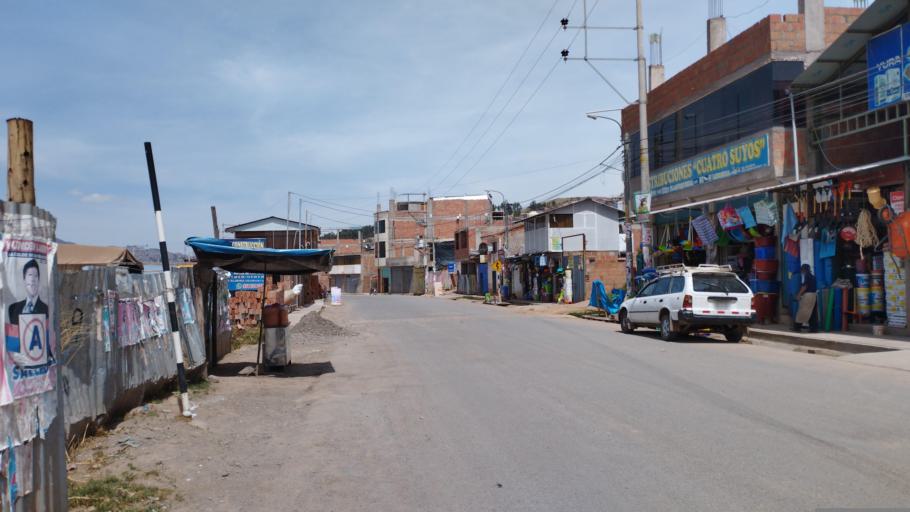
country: PE
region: Cusco
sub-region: Provincia de Cusco
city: Cusco
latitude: -13.5228
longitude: -71.9250
